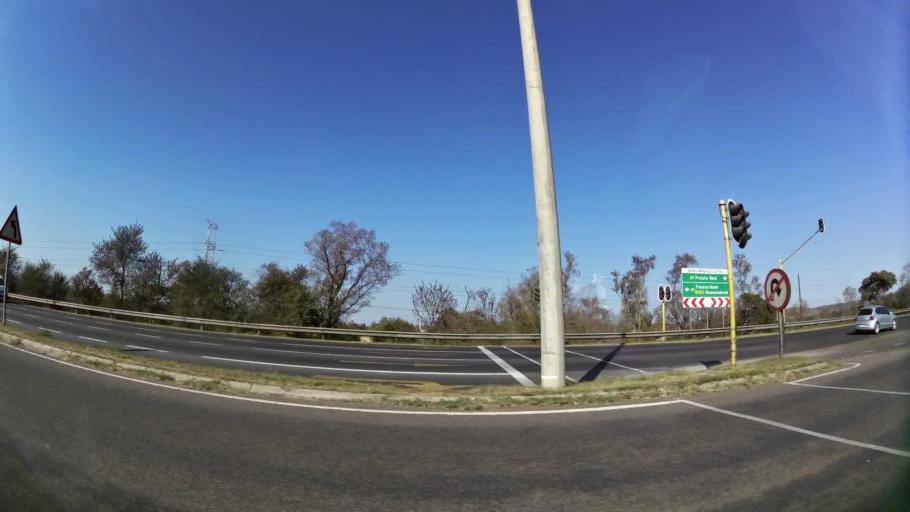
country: ZA
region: Gauteng
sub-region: City of Tshwane Metropolitan Municipality
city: Pretoria
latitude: -25.7125
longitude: 28.1715
